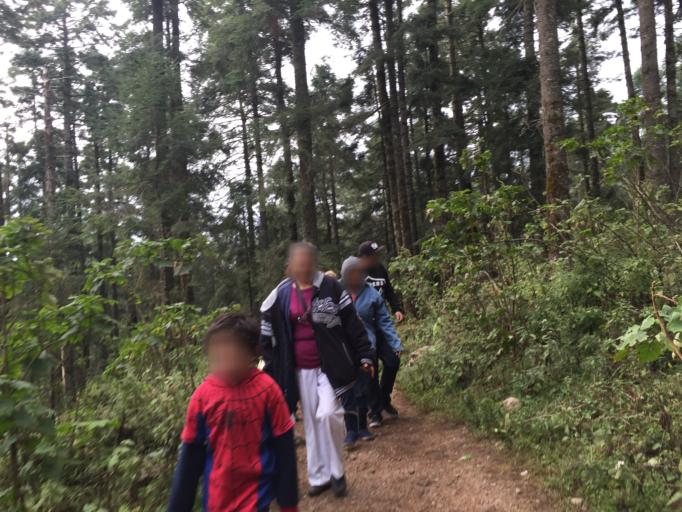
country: MX
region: Michoacan
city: Mineral de Angangueo
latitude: 19.6734
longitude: -100.2936
